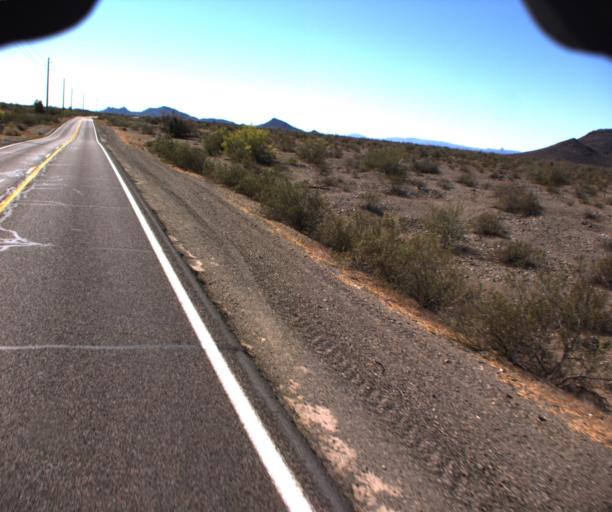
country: US
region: Arizona
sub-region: La Paz County
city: Salome
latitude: 33.7745
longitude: -113.7982
